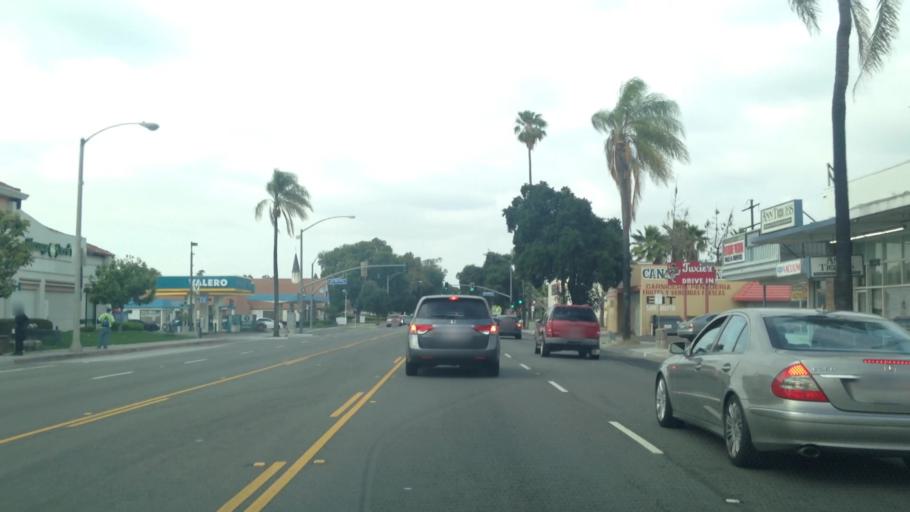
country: US
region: California
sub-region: Riverside County
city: Riverside
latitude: 33.9599
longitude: -117.3924
